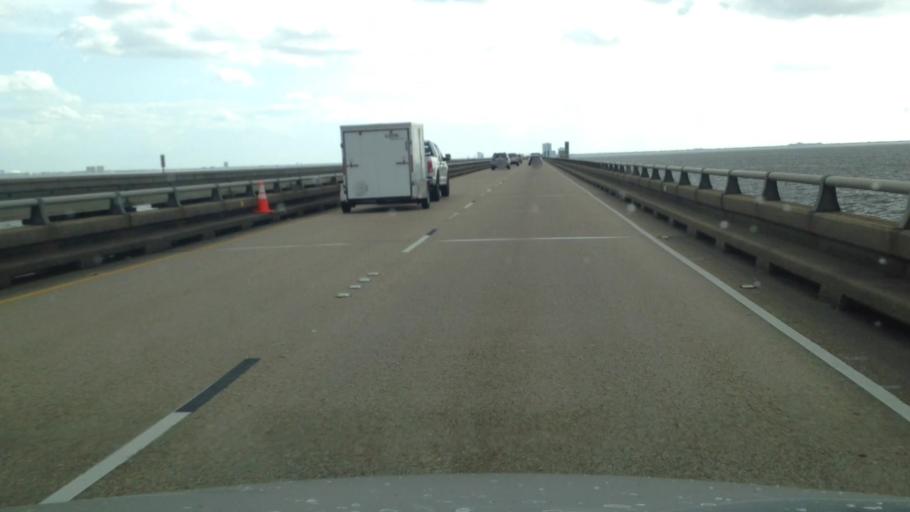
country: US
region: Louisiana
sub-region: Jefferson Parish
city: Metairie
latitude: 30.0944
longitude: -90.1414
